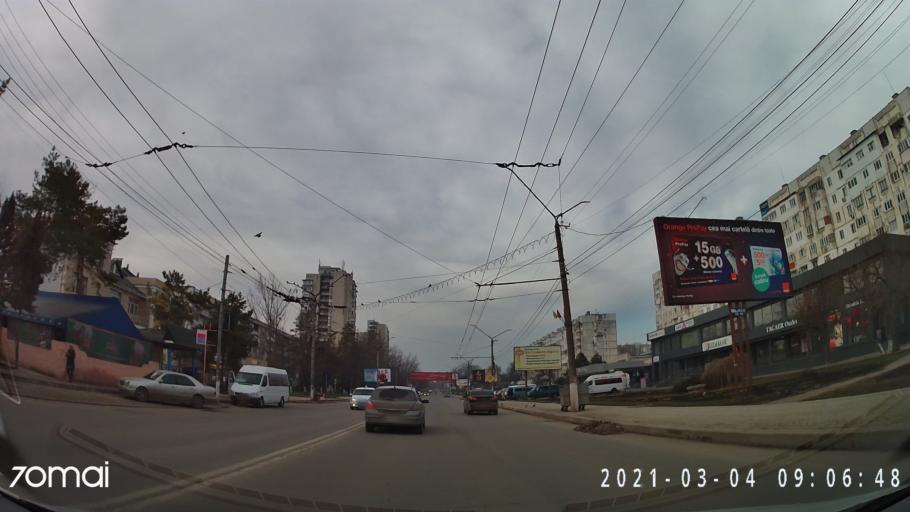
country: MD
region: Balti
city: Balti
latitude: 47.7682
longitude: 27.9405
